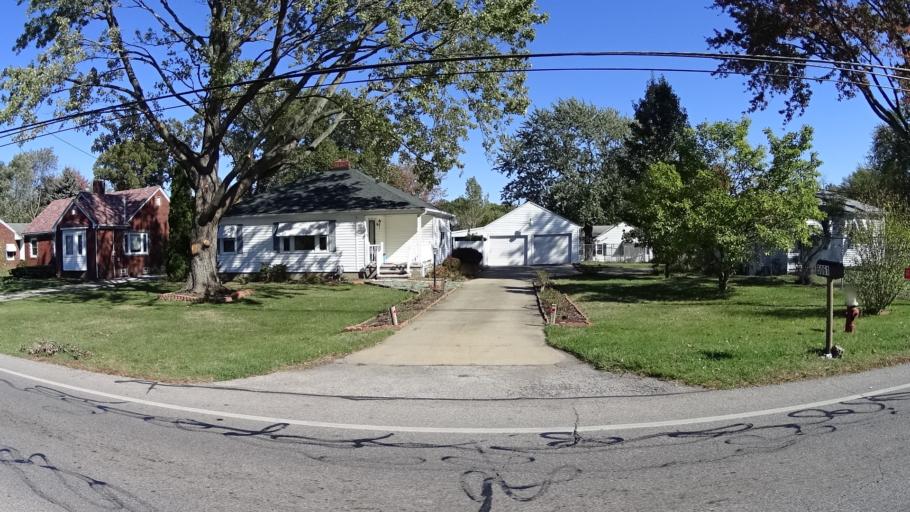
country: US
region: Ohio
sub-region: Lorain County
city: Lorain
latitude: 41.4222
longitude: -82.1456
